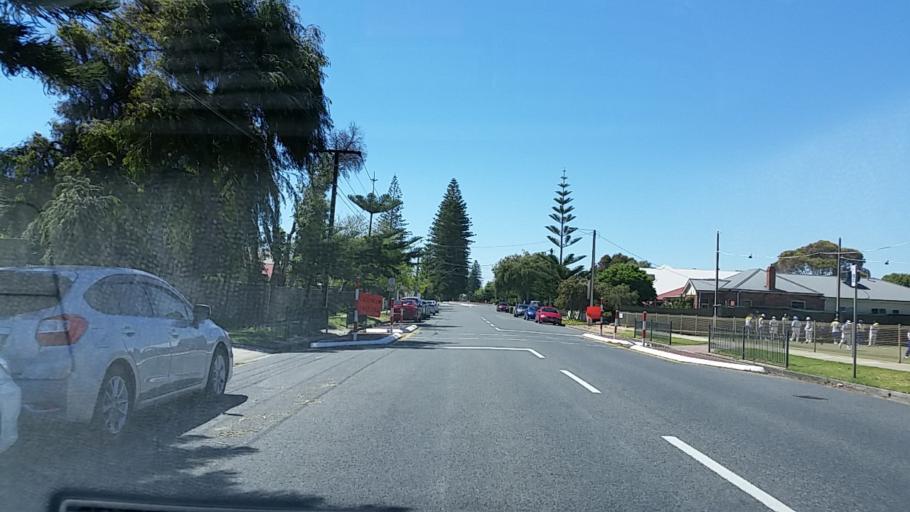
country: AU
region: South Australia
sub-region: Charles Sturt
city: Grange
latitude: -34.9067
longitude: 138.4927
